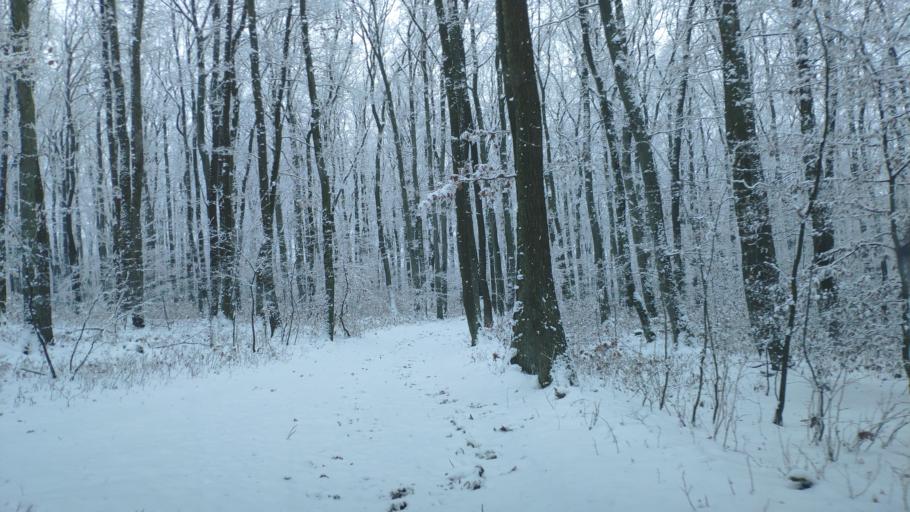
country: SK
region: Kosicky
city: Kosice
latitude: 48.6584
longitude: 21.1822
